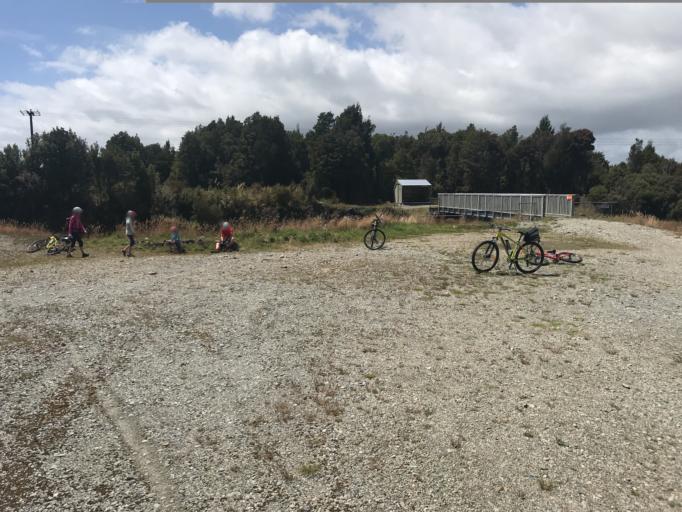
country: NZ
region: West Coast
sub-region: Westland District
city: Hokitika
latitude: -42.6940
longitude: 171.1897
